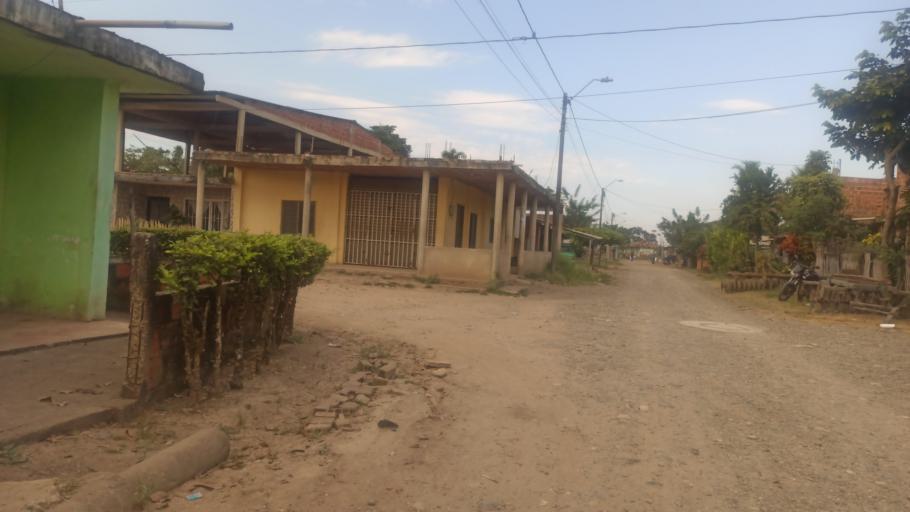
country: CO
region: Valle del Cauca
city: Jamundi
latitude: 3.1290
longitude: -76.5589
